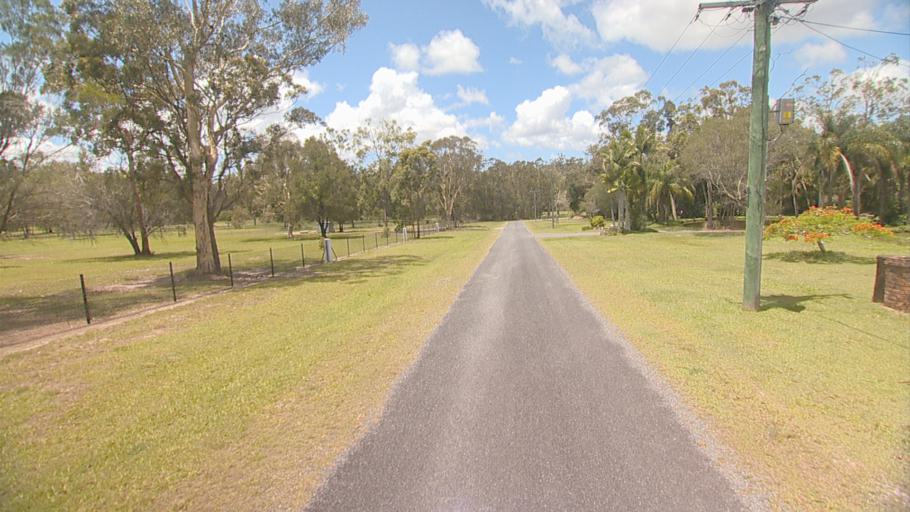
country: AU
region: Queensland
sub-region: Gold Coast
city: Yatala
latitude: -27.6577
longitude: 153.2470
